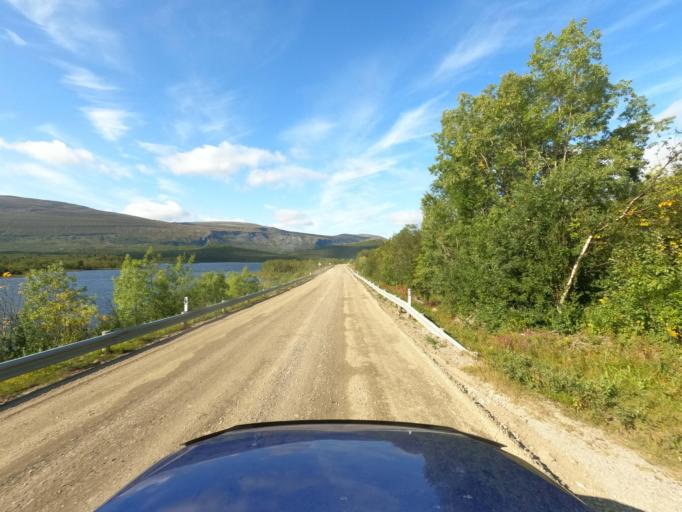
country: NO
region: Finnmark Fylke
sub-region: Porsanger
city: Lakselv
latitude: 69.8913
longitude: 24.9991
